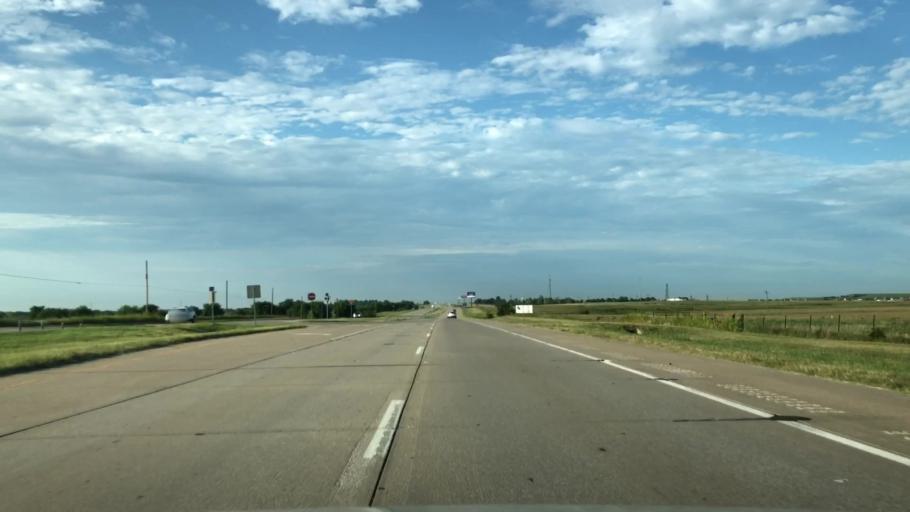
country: US
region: Oklahoma
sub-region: Osage County
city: Skiatook
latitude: 36.3808
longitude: -95.9206
